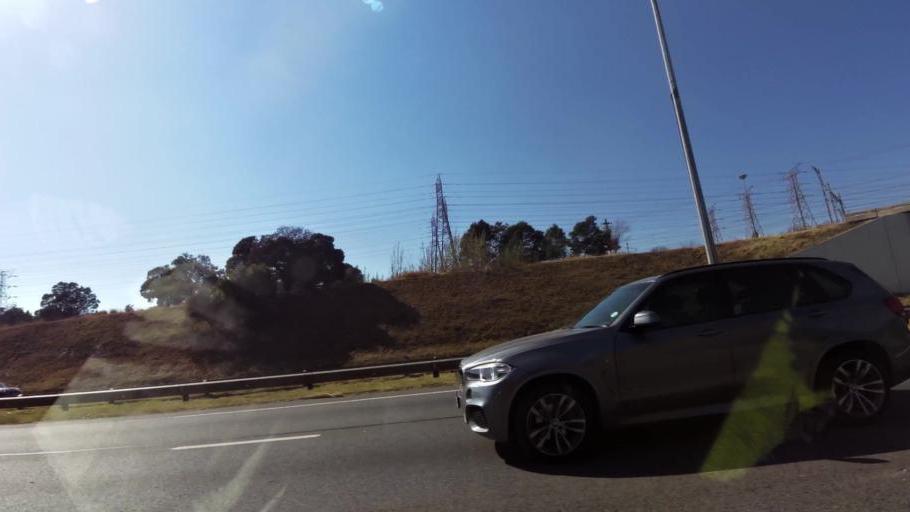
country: ZA
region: Gauteng
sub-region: City of Johannesburg Metropolitan Municipality
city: Roodepoort
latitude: -26.2007
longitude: 27.9537
